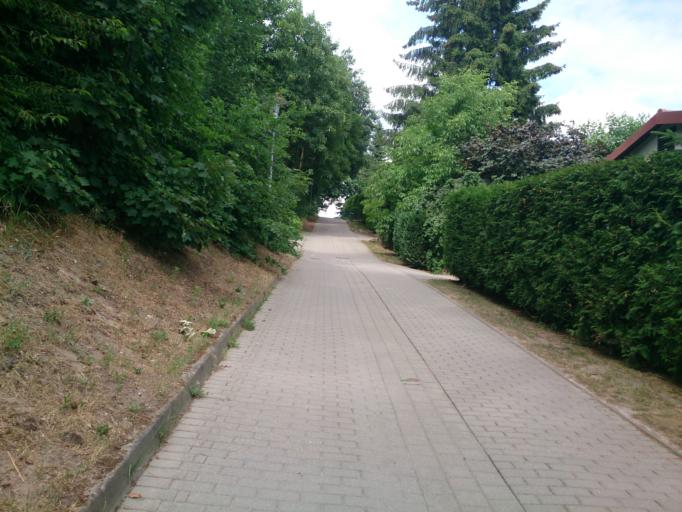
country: DE
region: Mecklenburg-Vorpommern
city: Waren
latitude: 53.5041
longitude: 12.6937
